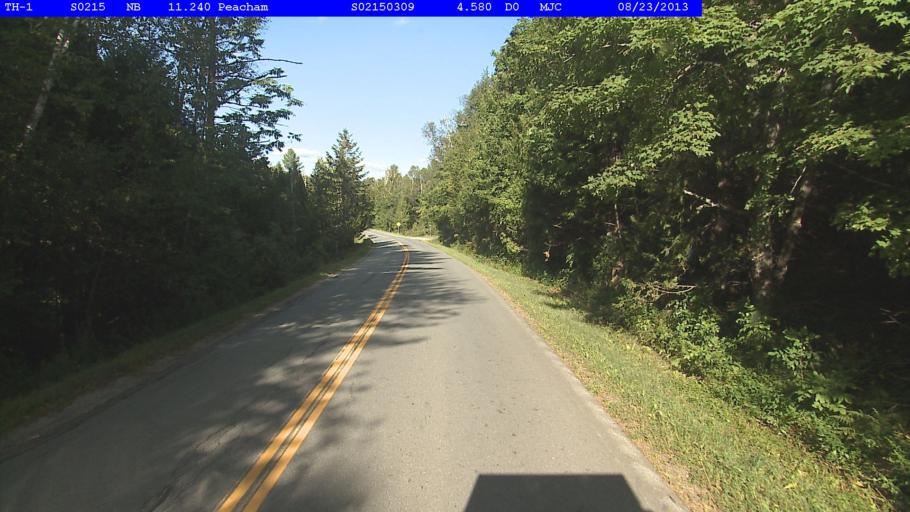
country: US
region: Vermont
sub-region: Caledonia County
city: Saint Johnsbury
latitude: 44.3602
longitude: -72.1706
